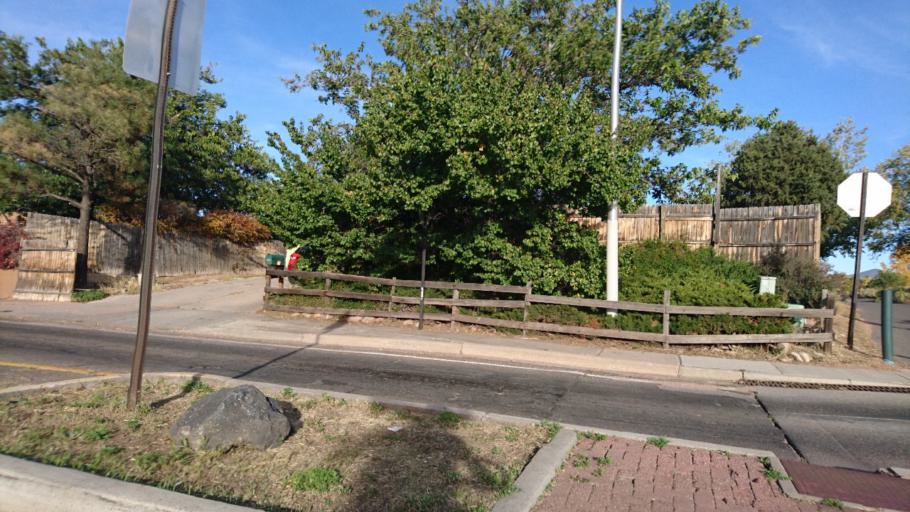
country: US
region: New Mexico
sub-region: Santa Fe County
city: Agua Fria
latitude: 35.6420
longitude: -105.9900
